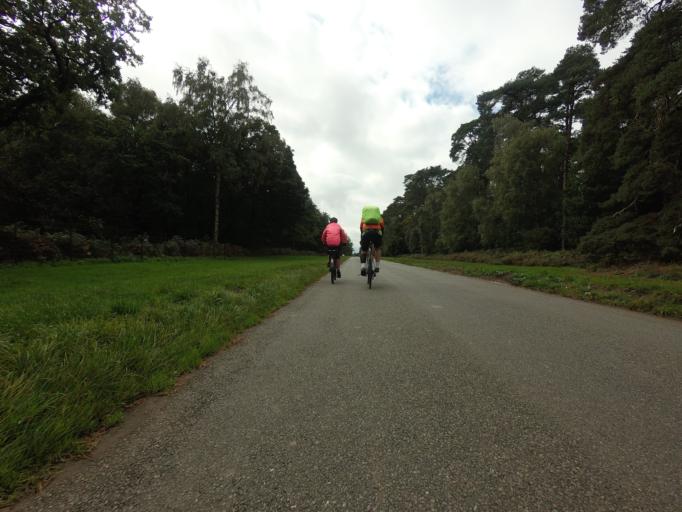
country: GB
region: England
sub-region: Norfolk
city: Dersingham
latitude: 52.8265
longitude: 0.5010
